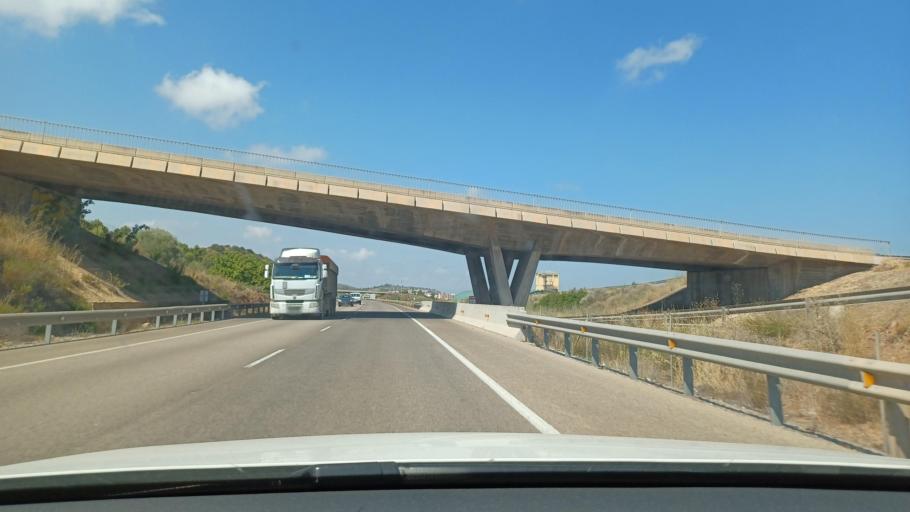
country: ES
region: Valencia
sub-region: Provincia de Castello
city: Almenara
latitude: 39.7542
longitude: -0.2149
